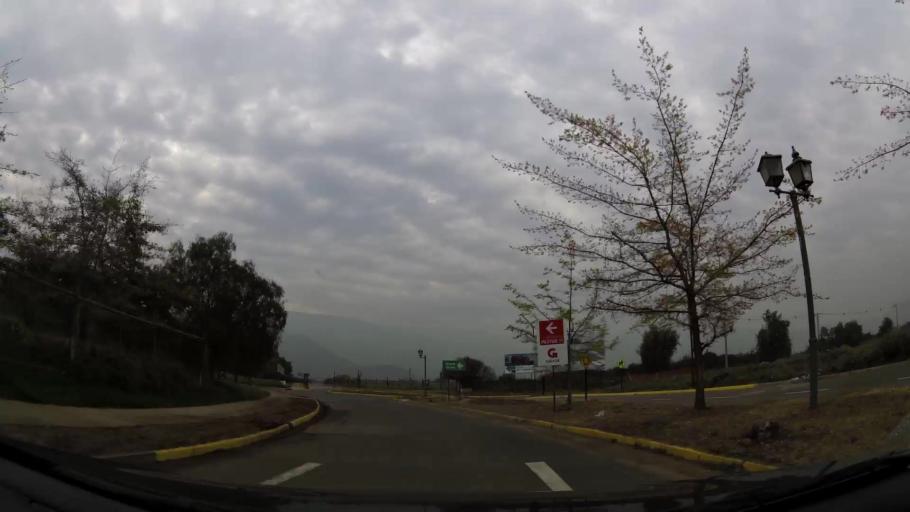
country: CL
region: Santiago Metropolitan
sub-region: Provincia de Chacabuco
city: Chicureo Abajo
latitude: -33.2191
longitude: -70.6644
